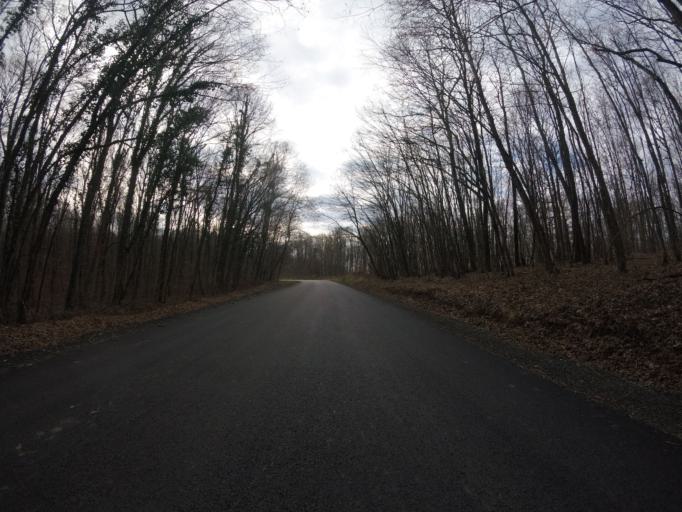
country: HR
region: Sisacko-Moslavacka
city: Glina
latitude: 45.5006
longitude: 16.0429
